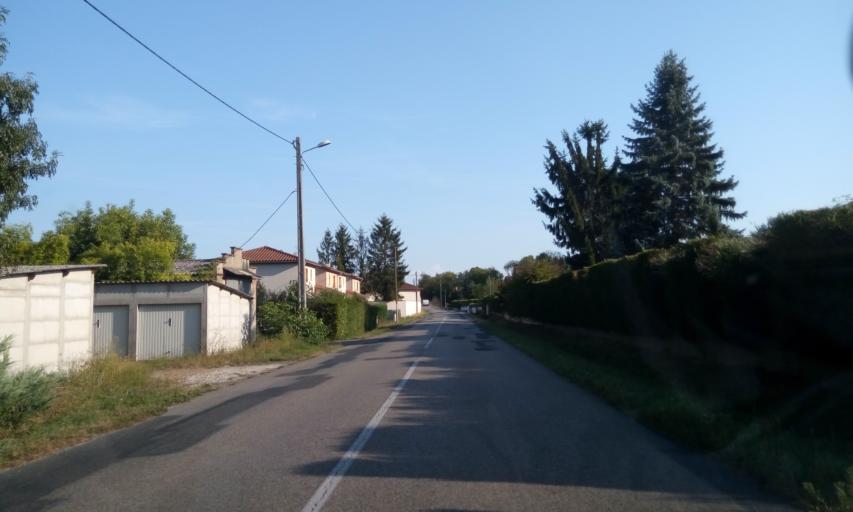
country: FR
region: Rhone-Alpes
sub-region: Departement de l'Ain
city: Villars-les-Dombes
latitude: 46.0078
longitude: 5.0234
